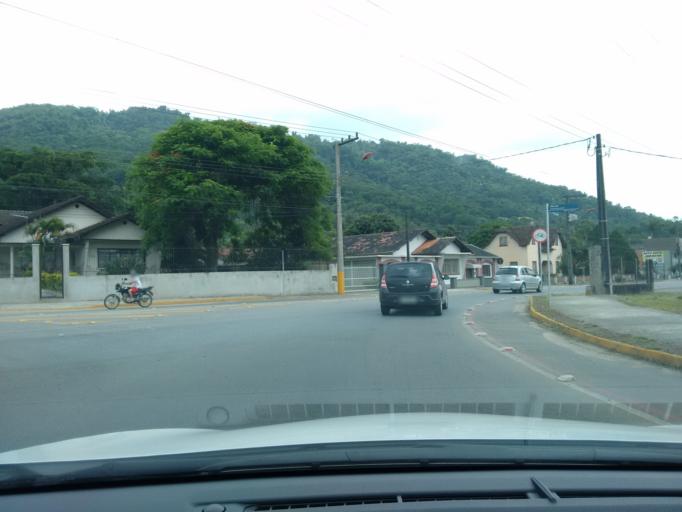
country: BR
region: Santa Catarina
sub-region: Jaragua Do Sul
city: Jaragua do Sul
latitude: -26.5063
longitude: -49.0943
